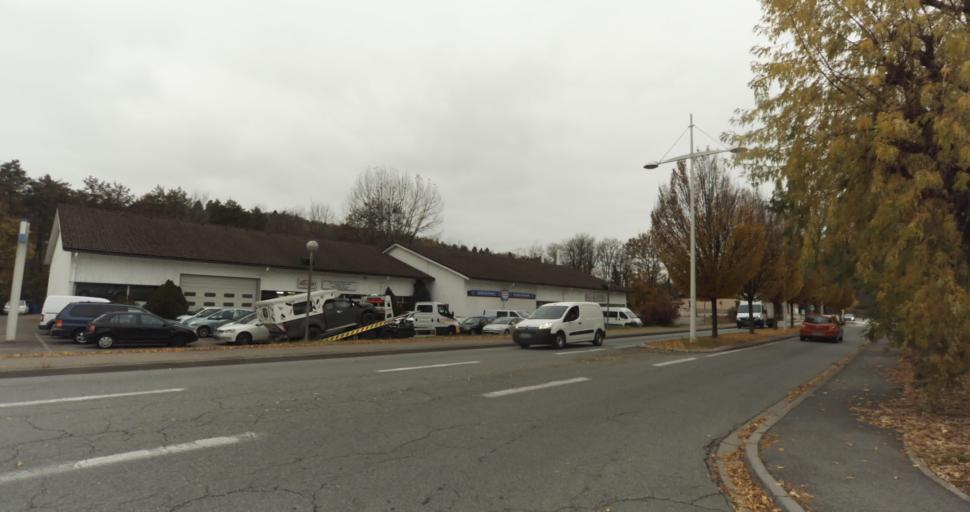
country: FR
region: Rhone-Alpes
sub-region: Departement de la Haute-Savoie
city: Epagny
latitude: 45.9288
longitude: 6.0836
